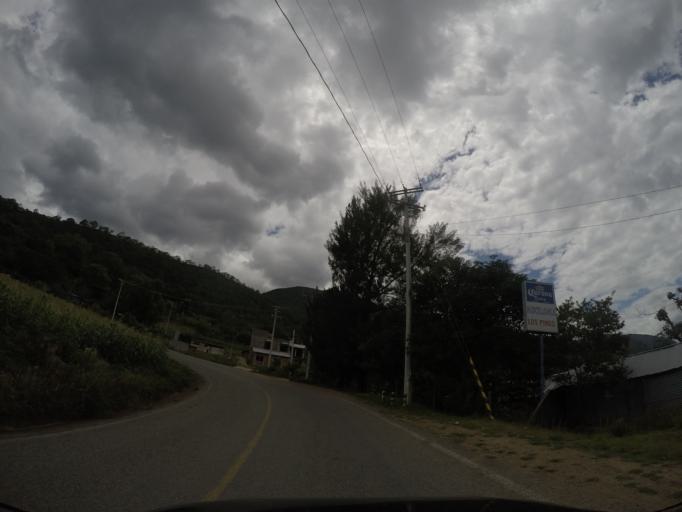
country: MX
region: Oaxaca
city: San Francisco Sola
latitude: 16.4920
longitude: -96.9851
